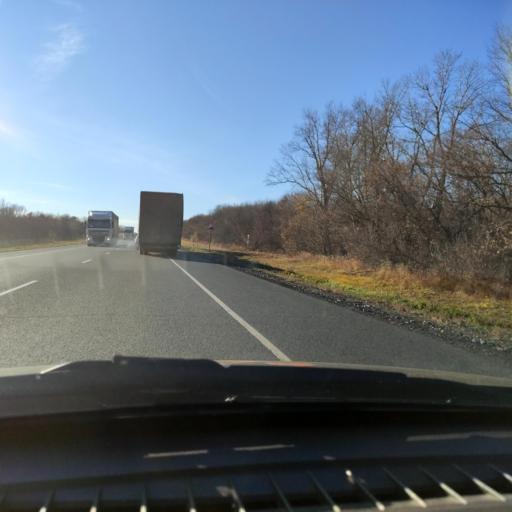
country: RU
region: Samara
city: Obsharovka
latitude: 53.2309
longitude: 48.9148
